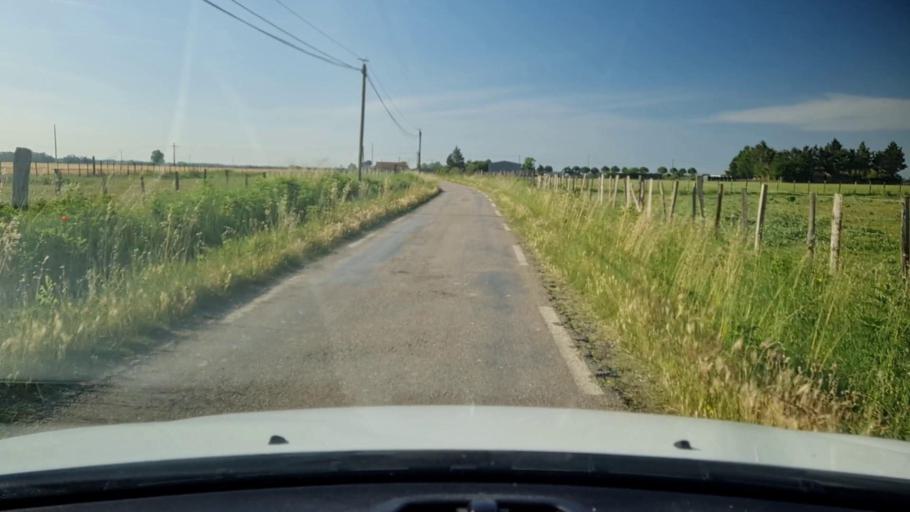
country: FR
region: Languedoc-Roussillon
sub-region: Departement du Gard
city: Le Cailar
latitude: 43.6532
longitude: 4.2177
